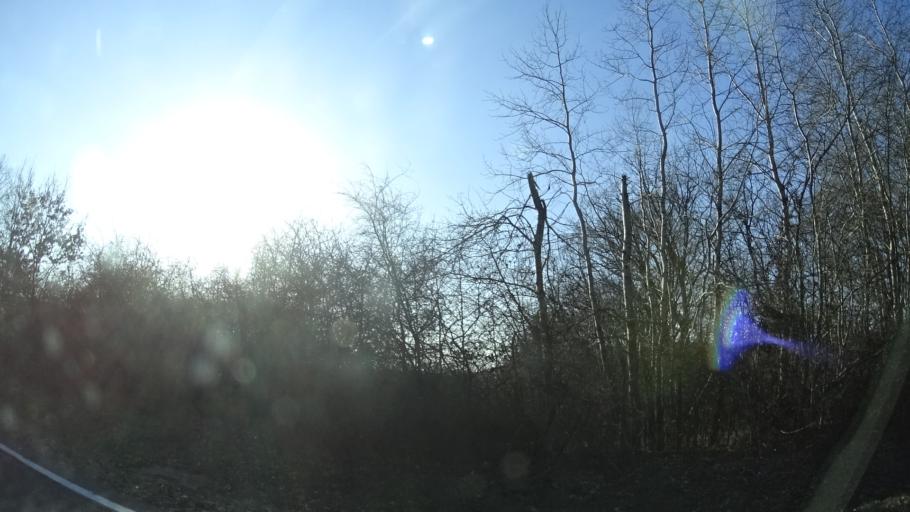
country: DE
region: Hesse
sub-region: Regierungsbezirk Darmstadt
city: Steinau an der Strasse
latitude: 50.3287
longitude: 9.4722
